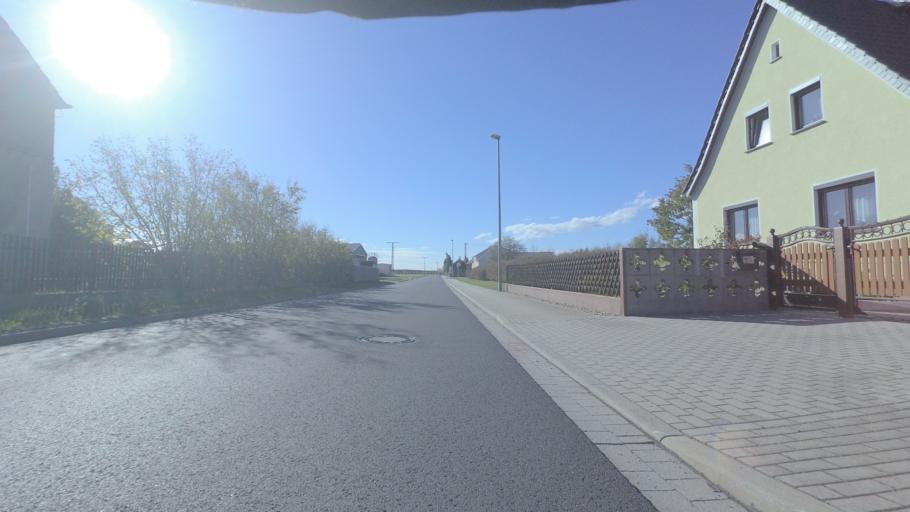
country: DE
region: Saxony
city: Nauwalde
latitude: 51.4420
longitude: 13.3657
